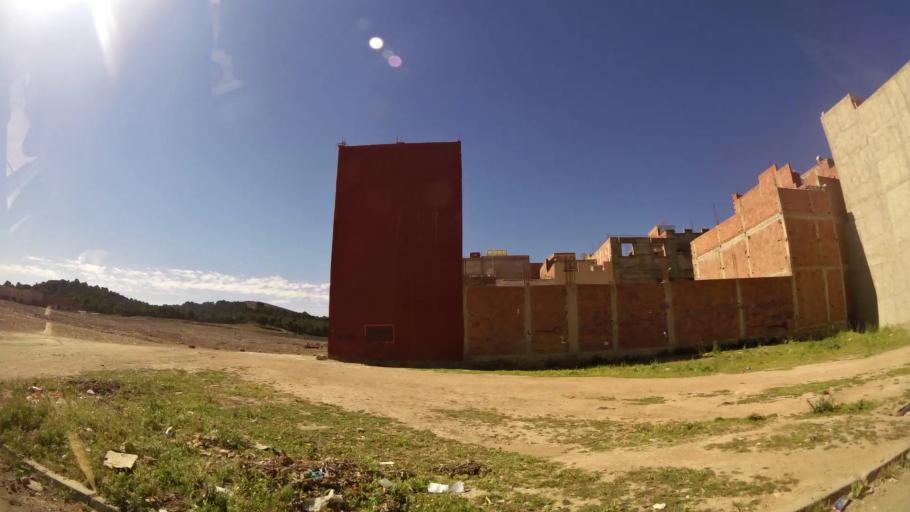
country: MA
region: Oriental
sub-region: Oujda-Angad
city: Oujda
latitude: 34.6498
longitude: -1.8809
